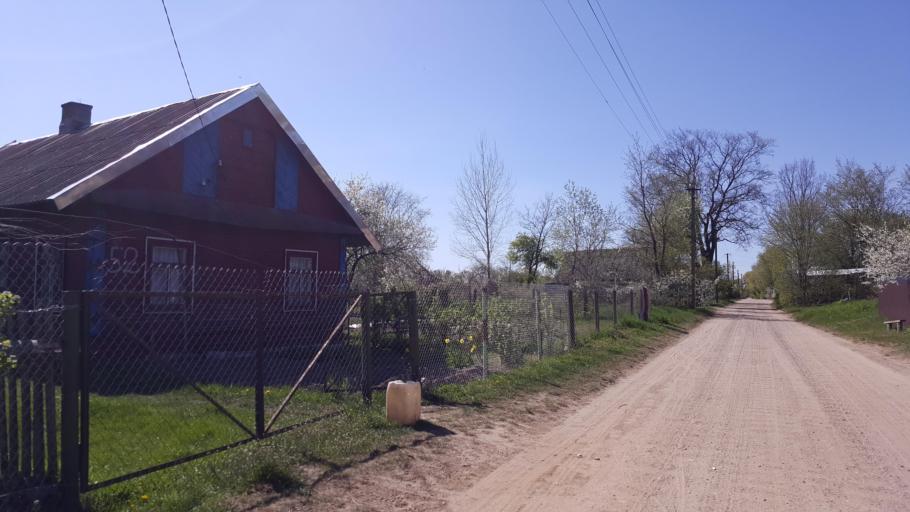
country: BY
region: Brest
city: Kamyanyets
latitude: 52.4525
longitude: 23.8872
